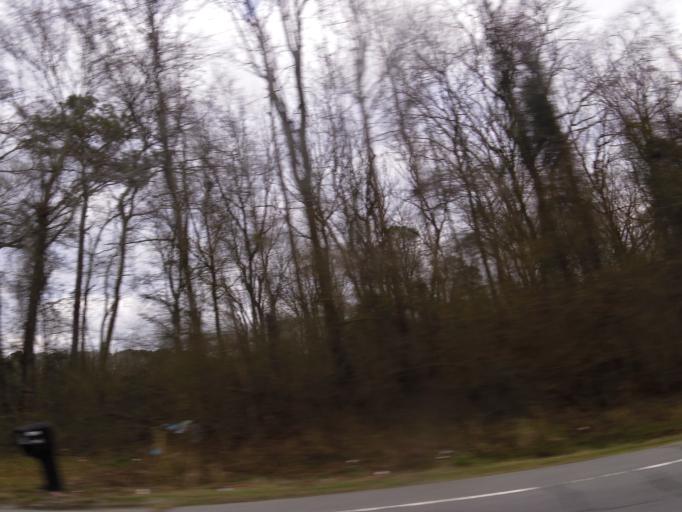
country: US
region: North Carolina
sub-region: Edgecombe County
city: Pinetops
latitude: 35.8296
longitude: -77.6589
